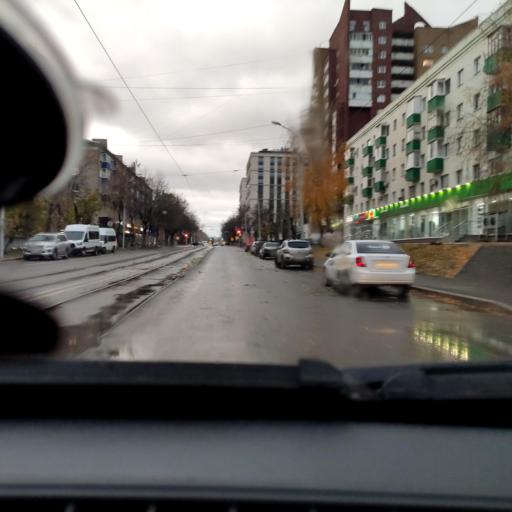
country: RU
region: Bashkortostan
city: Ufa
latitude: 54.7444
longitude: 55.9577
